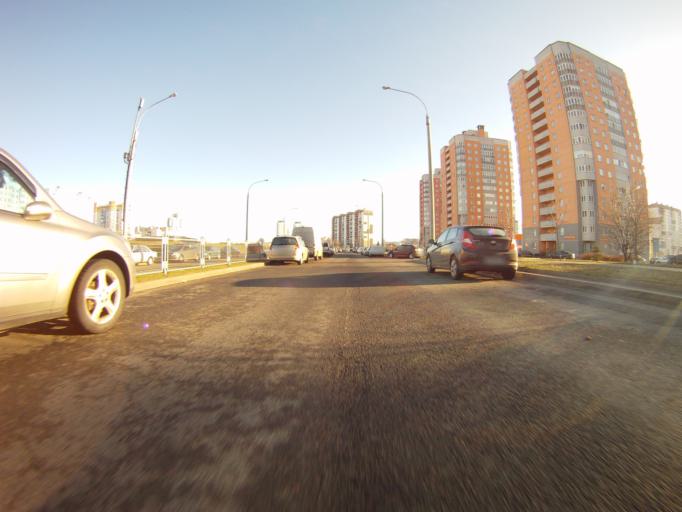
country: BY
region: Minsk
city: Novoye Medvezhino
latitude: 53.8765
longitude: 27.4504
